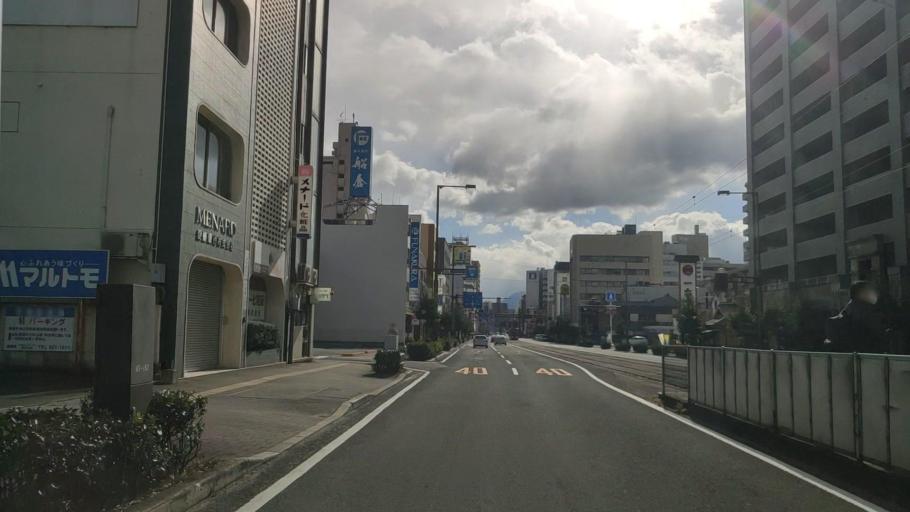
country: JP
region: Ehime
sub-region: Shikoku-chuo Shi
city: Matsuyama
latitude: 33.8444
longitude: 132.7754
